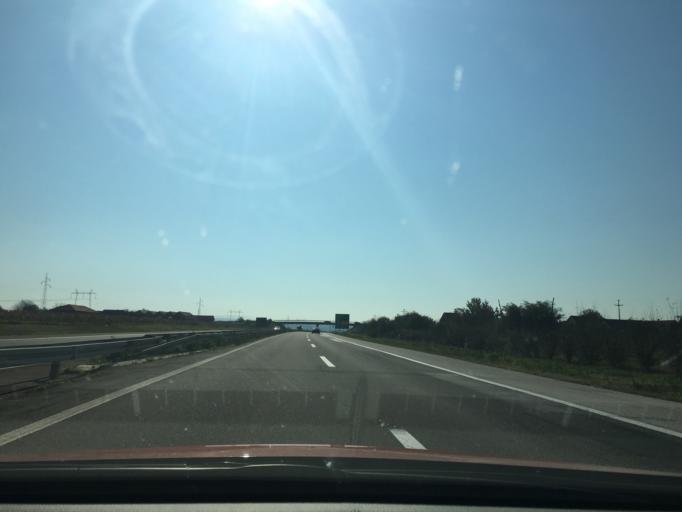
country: RS
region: Central Serbia
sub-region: Pomoravski Okrug
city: Cuprija
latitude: 43.9464
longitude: 21.3809
